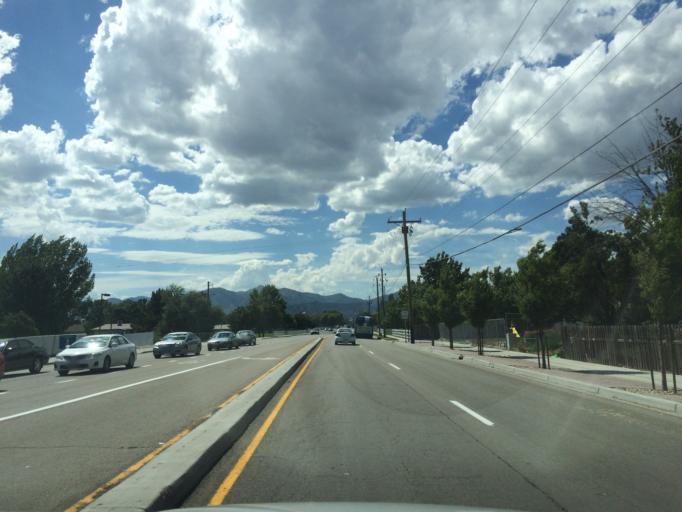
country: US
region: Utah
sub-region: Salt Lake County
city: Kearns
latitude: 40.6387
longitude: -111.9785
